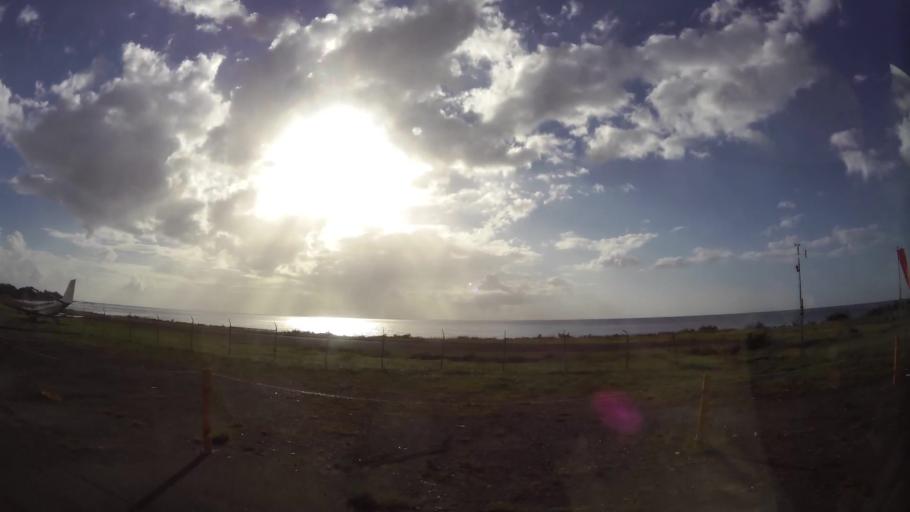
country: DM
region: Saint Paul
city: Mahaut
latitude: 15.3410
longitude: -61.3918
